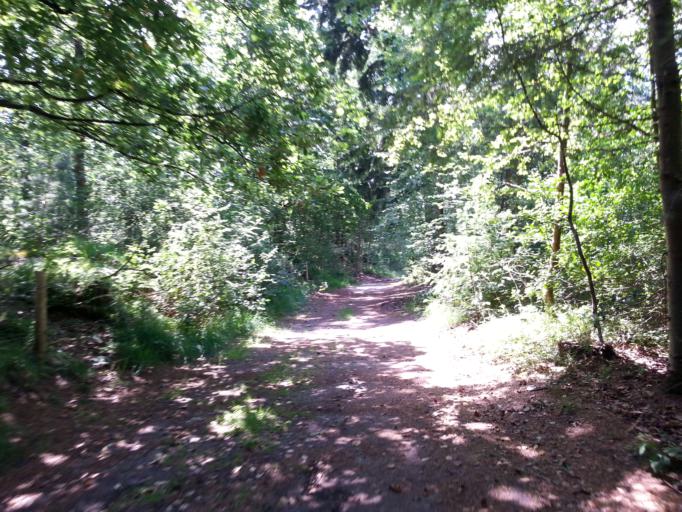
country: NL
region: Utrecht
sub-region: Gemeente Amersfoort
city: Randenbroek
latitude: 52.1186
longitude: 5.3936
